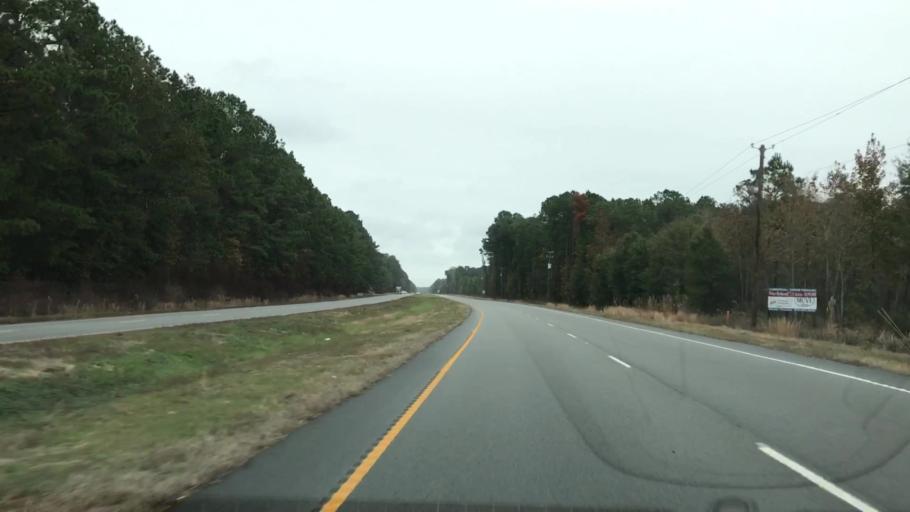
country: US
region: South Carolina
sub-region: Charleston County
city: Awendaw
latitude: 33.1020
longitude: -79.4668
